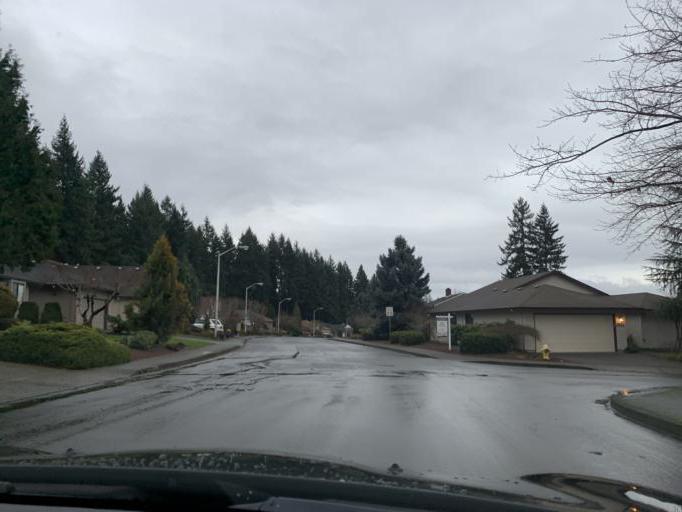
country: US
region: Washington
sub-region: Clark County
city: Mill Plain
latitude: 45.5999
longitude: -122.5115
